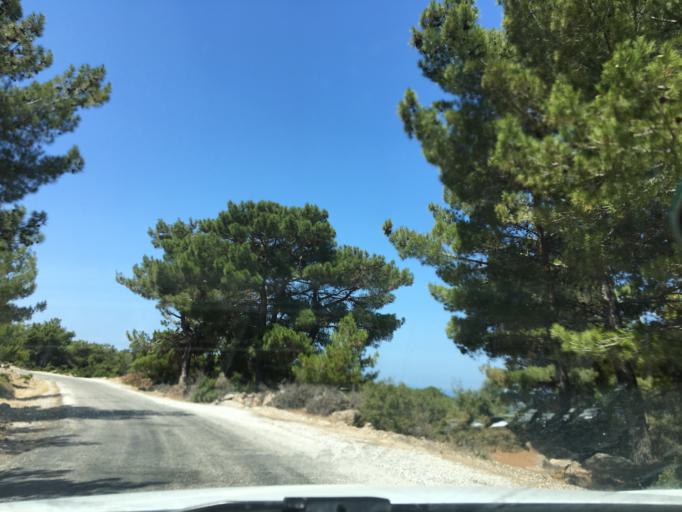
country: TR
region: Canakkale
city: Gulpinar
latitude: 39.4983
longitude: 26.1288
